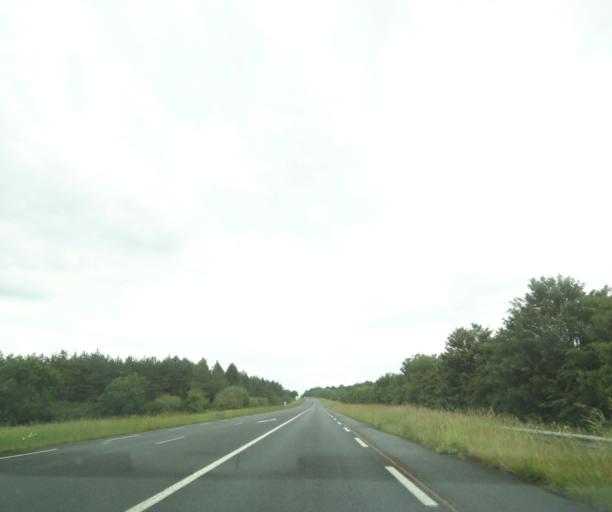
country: FR
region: Poitou-Charentes
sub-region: Departement des Deux-Sevres
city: Airvault
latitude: 46.7879
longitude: -0.2154
